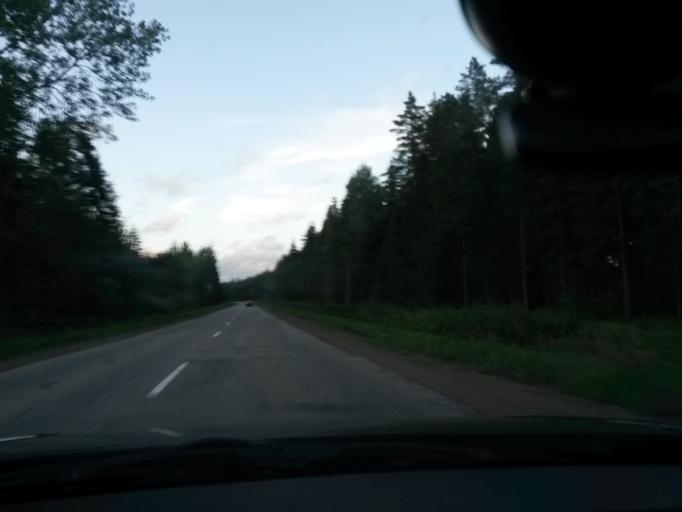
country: LV
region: Jekabpils Rajons
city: Jekabpils
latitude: 56.6723
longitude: 25.9757
